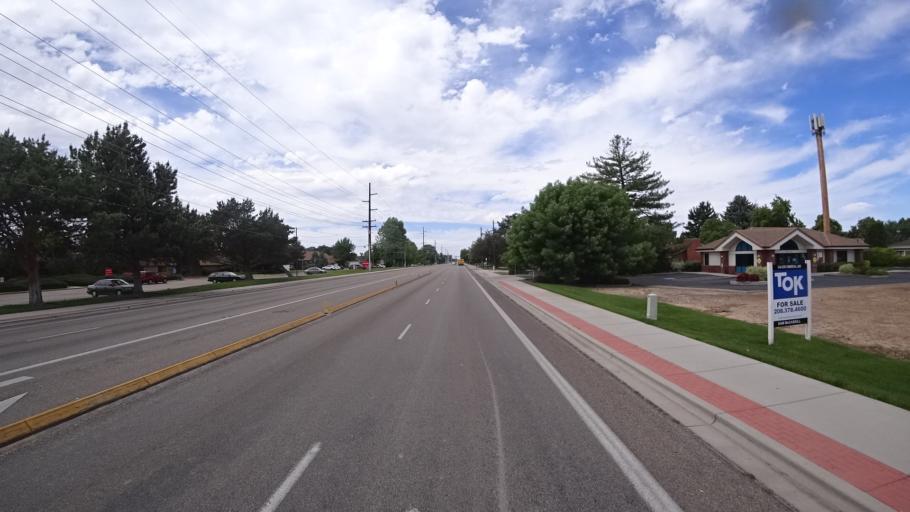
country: US
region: Idaho
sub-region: Ada County
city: Garden City
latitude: 43.6340
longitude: -116.2844
